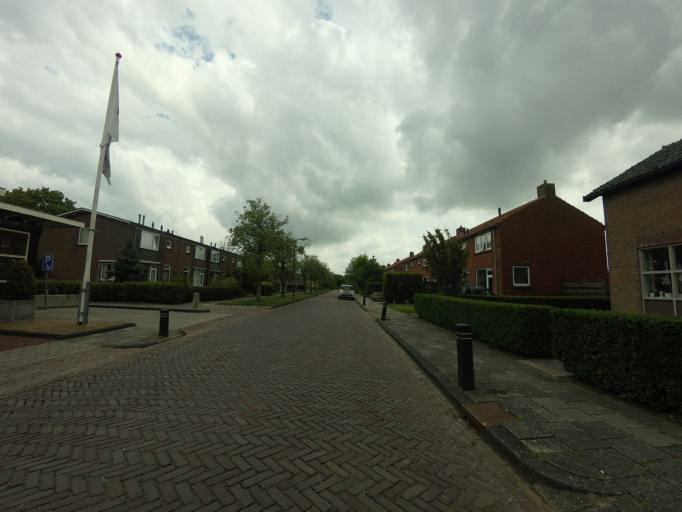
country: NL
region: Friesland
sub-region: Gemeente Littenseradiel
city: Wommels
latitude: 53.1080
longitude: 5.5905
